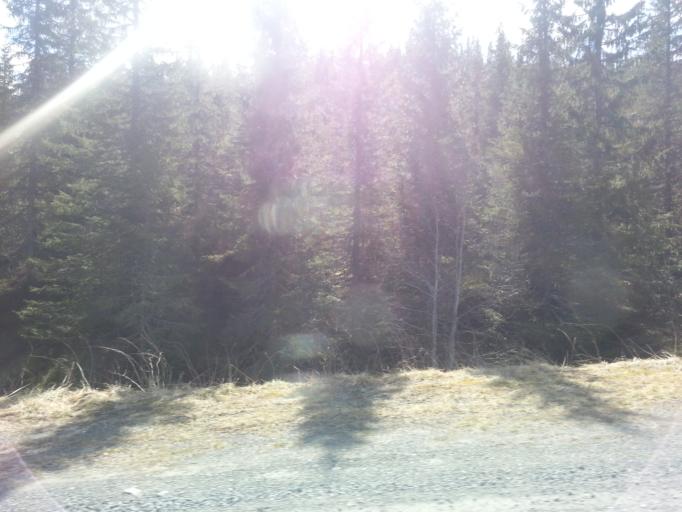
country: NO
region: Nord-Trondelag
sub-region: Levanger
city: Skogn
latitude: 63.5869
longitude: 11.1041
